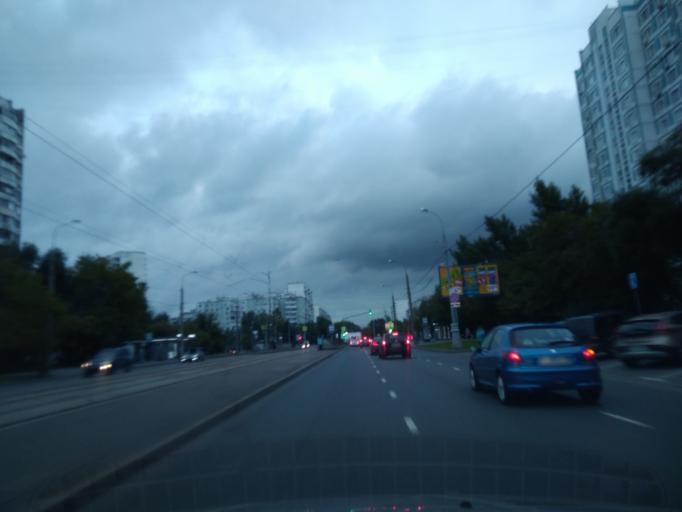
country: RU
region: Moscow
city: Strogino
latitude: 55.8107
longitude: 37.3977
